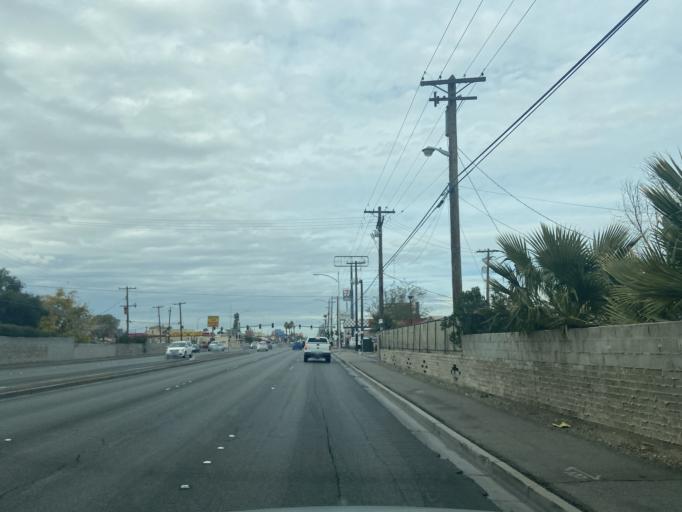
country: US
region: Nevada
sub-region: Clark County
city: Las Vegas
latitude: 36.1874
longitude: -115.1848
